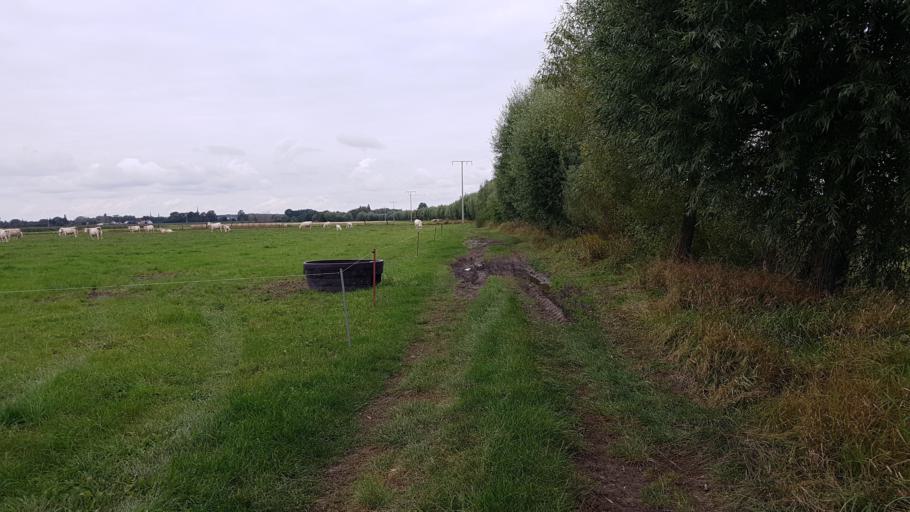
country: DE
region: Brandenburg
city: Doberlug-Kirchhain
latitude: 51.6123
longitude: 13.5760
